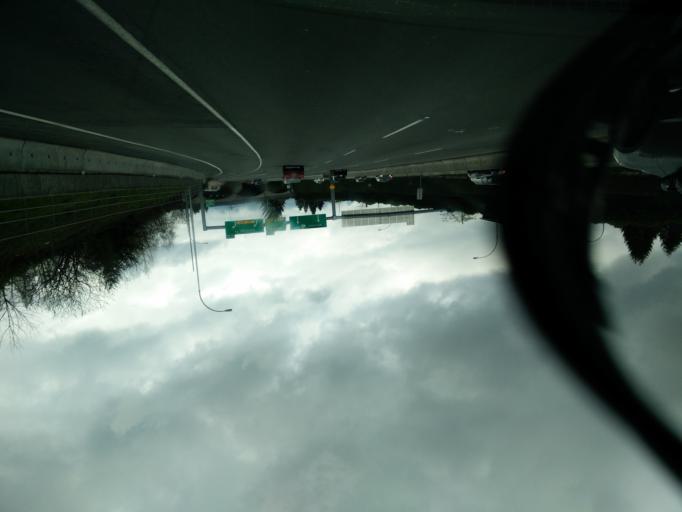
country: CA
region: British Columbia
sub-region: Fraser Valley Regional District
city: North Vancouver
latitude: 49.2750
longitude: -123.0310
